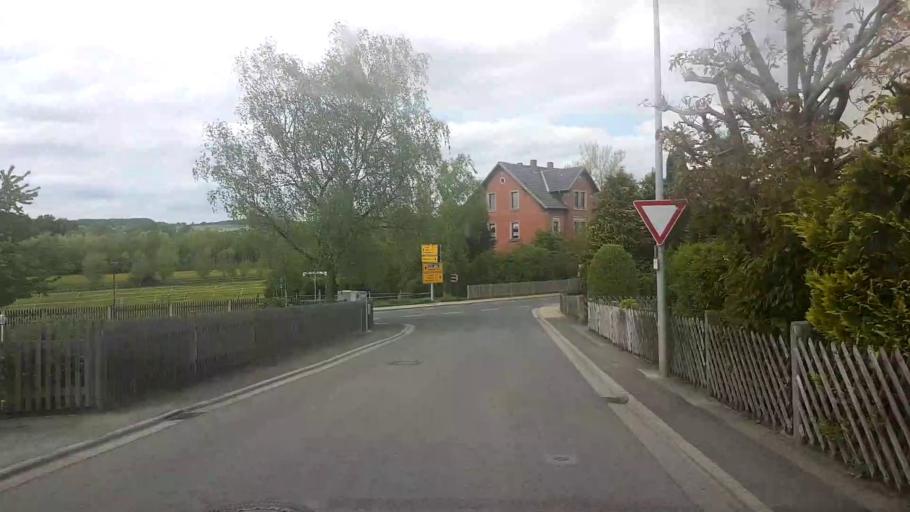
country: DE
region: Bavaria
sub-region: Upper Franconia
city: Untersiemau
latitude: 50.2040
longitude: 10.9752
